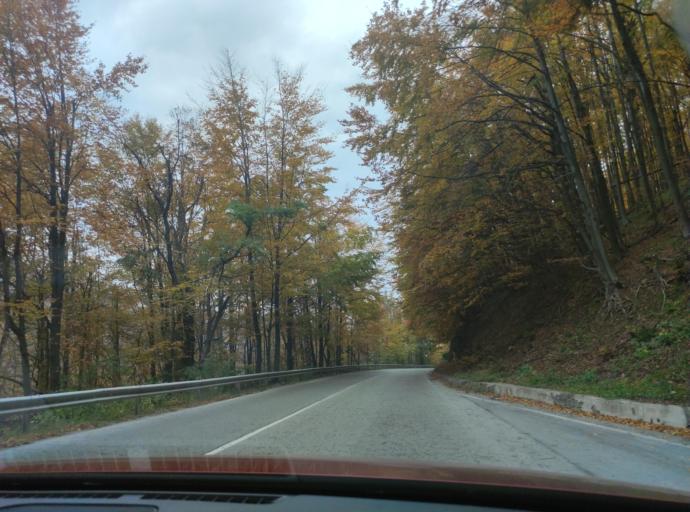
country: BG
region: Montana
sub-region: Obshtina Berkovitsa
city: Berkovitsa
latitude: 43.1442
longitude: 23.1434
